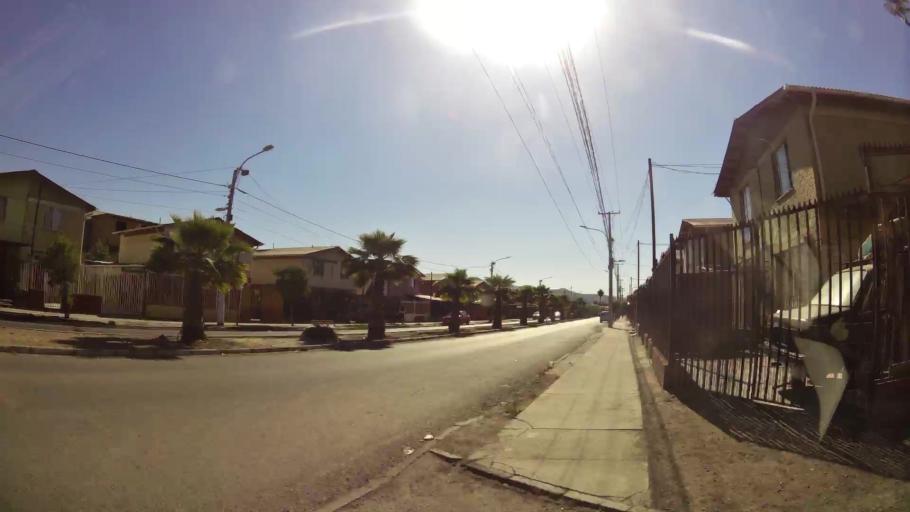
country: CL
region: Santiago Metropolitan
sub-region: Provincia de Maipo
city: San Bernardo
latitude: -33.5866
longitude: -70.6719
